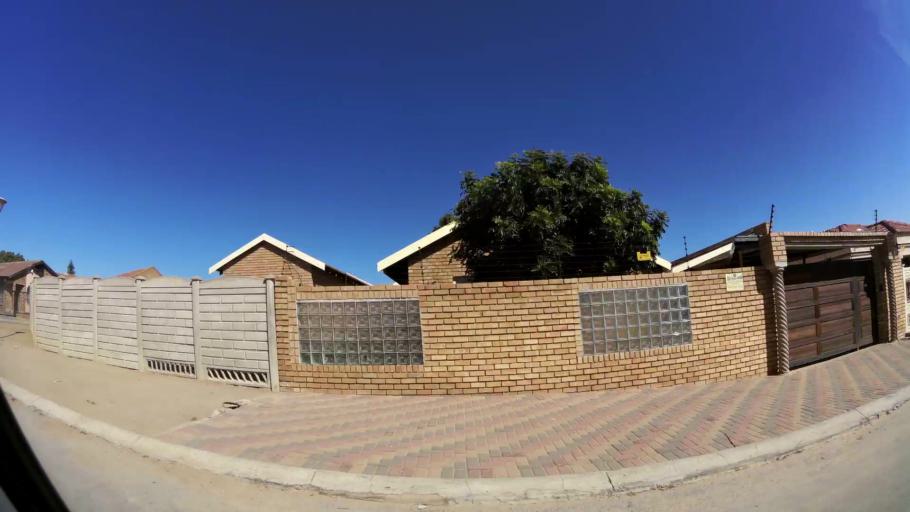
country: ZA
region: Limpopo
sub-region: Capricorn District Municipality
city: Polokwane
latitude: -23.8741
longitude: 29.4151
